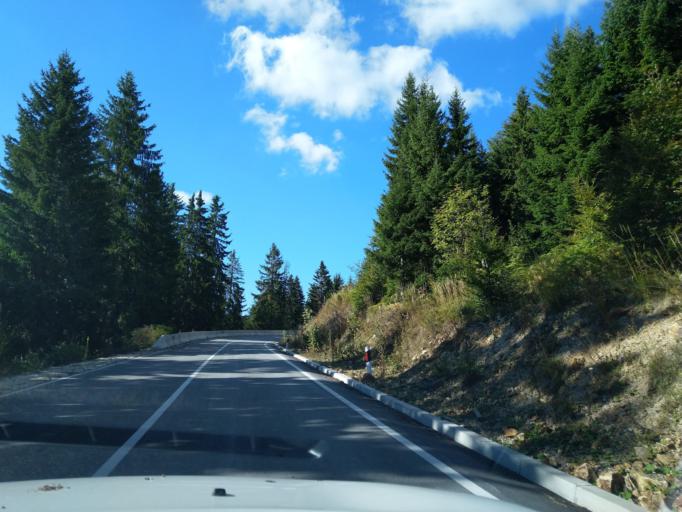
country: RS
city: Sokolovica
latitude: 43.3036
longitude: 20.3053
